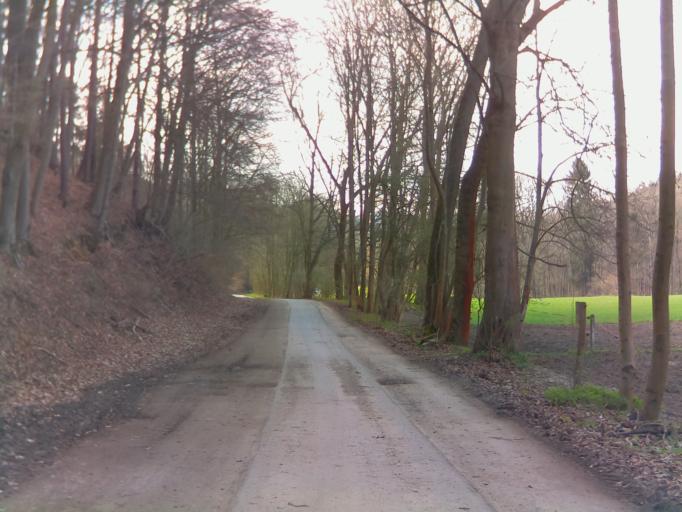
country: DE
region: Thuringia
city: Altenberga
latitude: 50.8291
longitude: 11.5253
